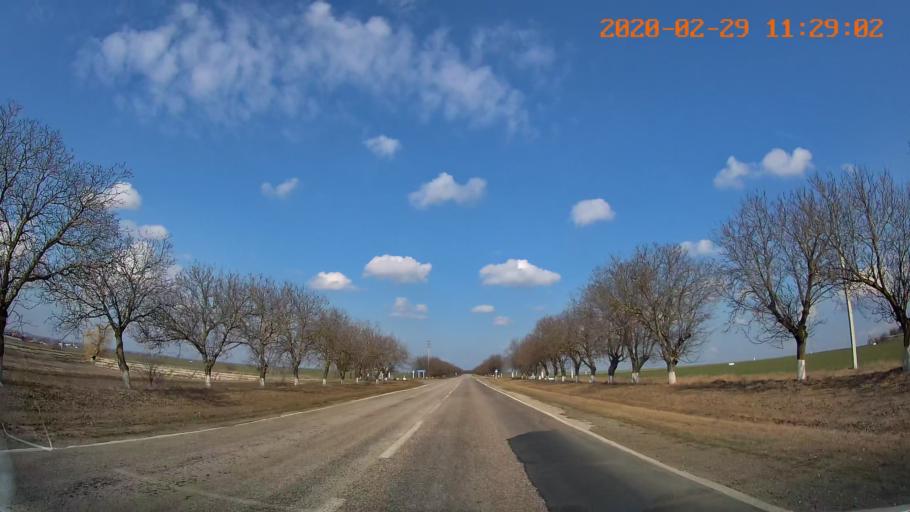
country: MD
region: Telenesti
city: Cocieri
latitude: 47.4883
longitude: 29.1289
